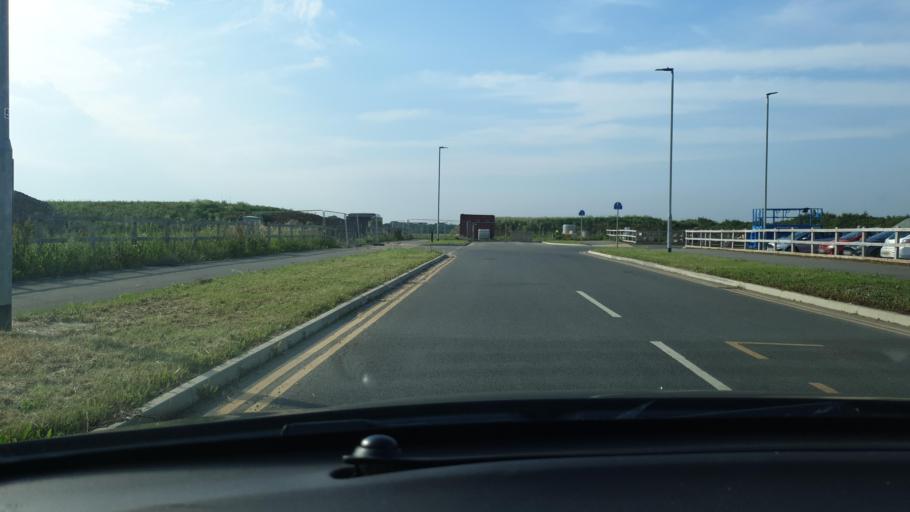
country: GB
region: England
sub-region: Essex
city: Little Clacton
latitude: 51.8119
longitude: 1.1428
